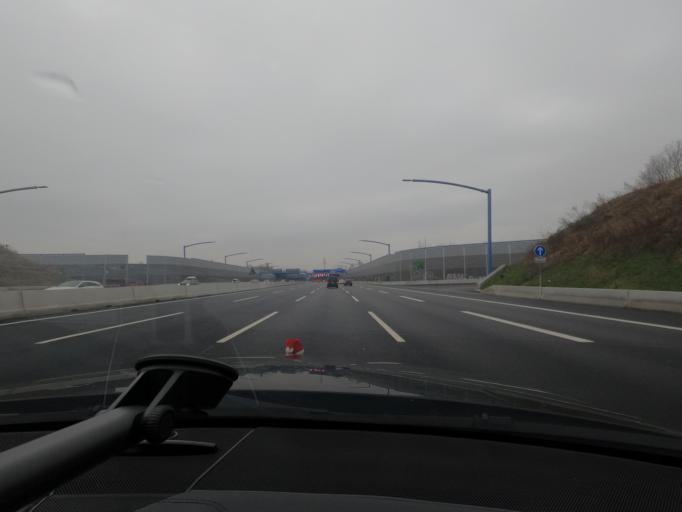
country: DE
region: Hamburg
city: Eidelstedt
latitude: 53.6076
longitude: 9.9182
